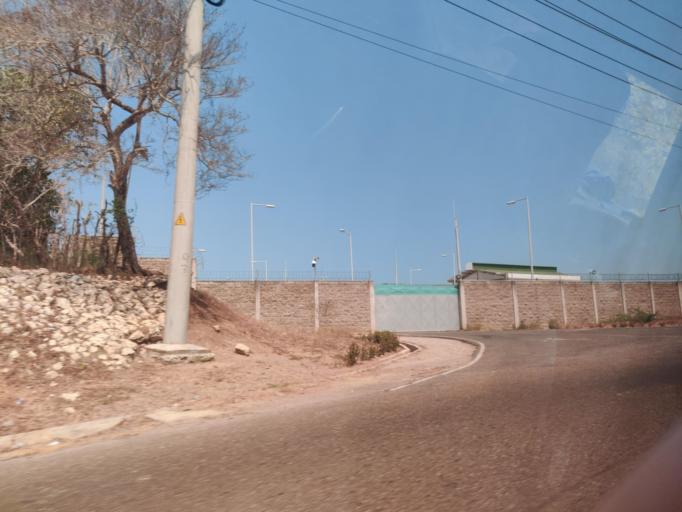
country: CO
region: Bolivar
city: Turbana
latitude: 10.2707
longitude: -75.5511
